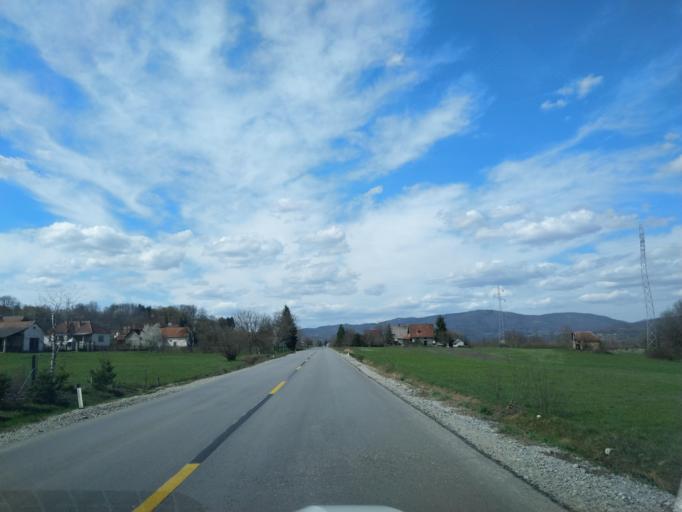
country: RS
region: Central Serbia
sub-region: Zlatiborski Okrug
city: Arilje
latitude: 43.8099
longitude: 20.0908
